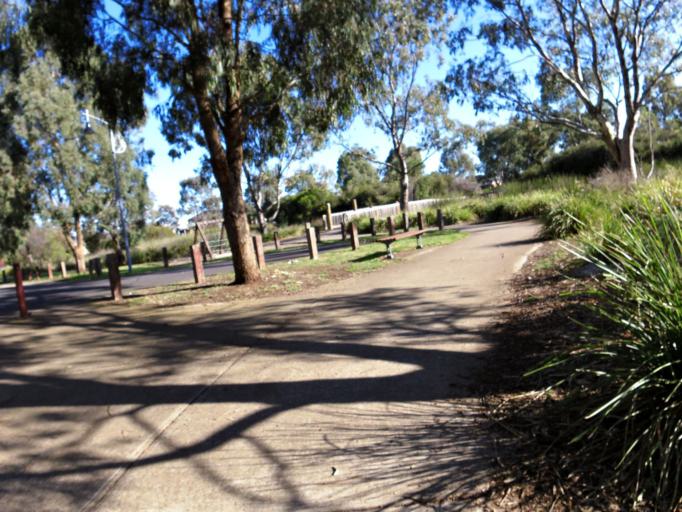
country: AU
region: Victoria
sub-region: Wyndham
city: Hoppers Crossing
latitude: -37.8449
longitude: 144.7007
